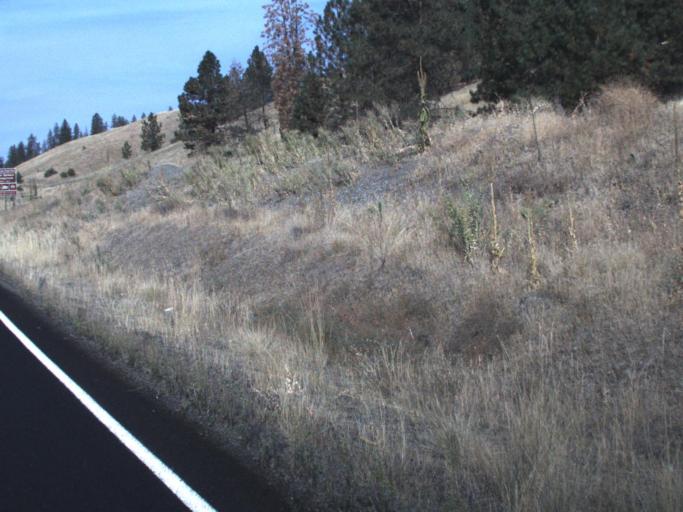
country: US
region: Washington
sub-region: Spokane County
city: Fairchild Air Force Base
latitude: 47.8380
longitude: -117.7573
